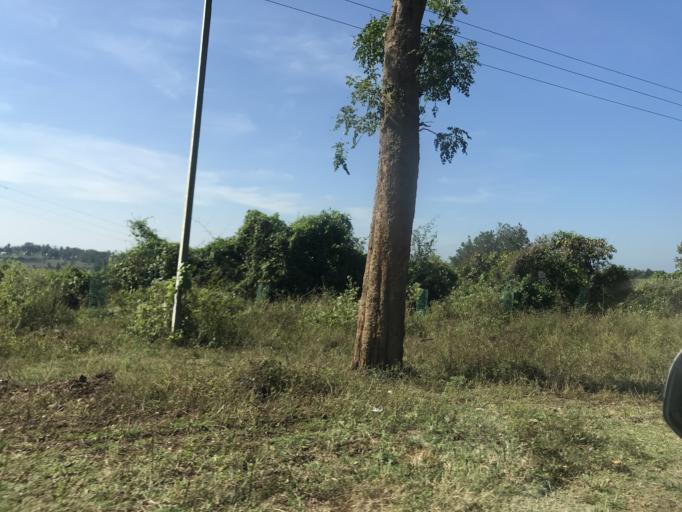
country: IN
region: Karnataka
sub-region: Mysore
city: Heggadadevankote
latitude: 12.0161
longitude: 76.2658
